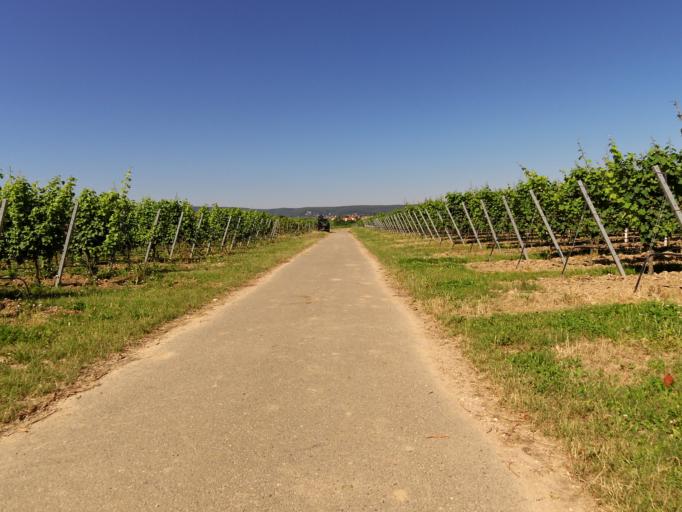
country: DE
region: Rheinland-Pfalz
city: Bissersheim
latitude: 49.5234
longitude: 8.2044
